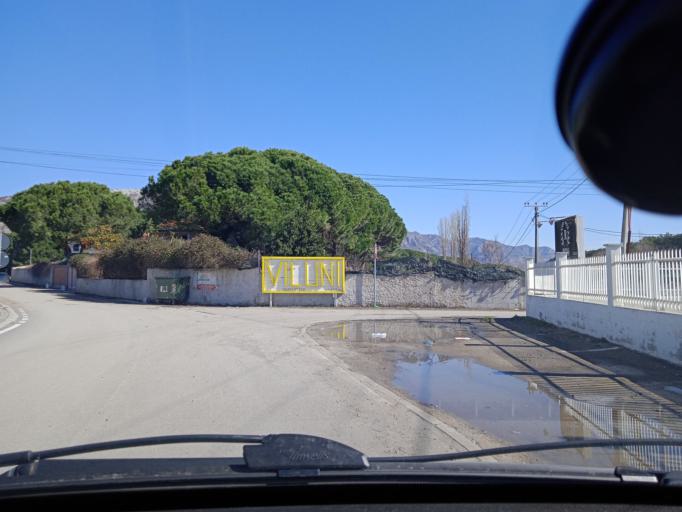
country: AL
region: Shkoder
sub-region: Rrethi i Shkodres
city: Velipoje
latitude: 41.8623
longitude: 19.4395
